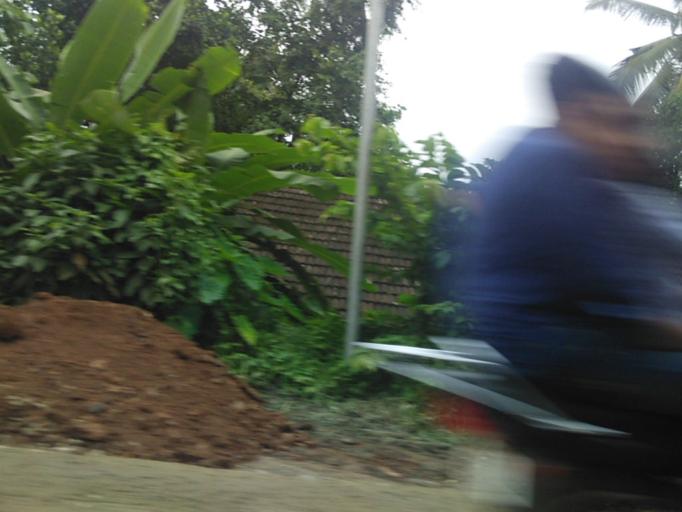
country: IN
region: Kerala
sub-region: Kozhikode
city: Kunnamangalam
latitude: 11.3073
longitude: 75.8825
